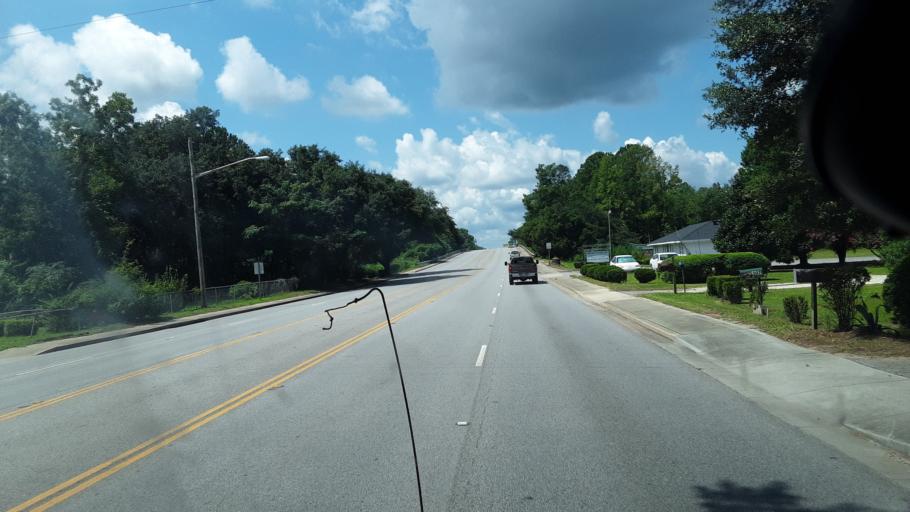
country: US
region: South Carolina
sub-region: Berkeley County
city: Moncks Corner
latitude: 33.2003
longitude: -79.9984
